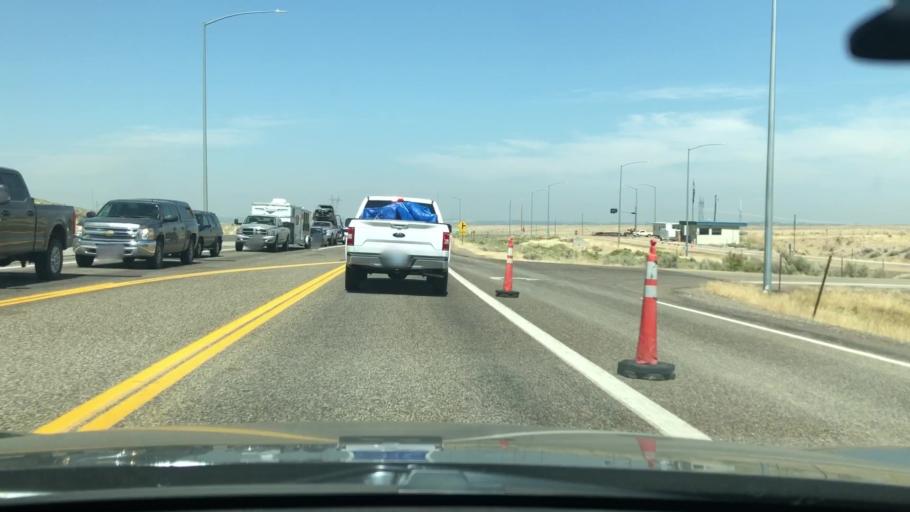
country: US
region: Idaho
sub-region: Owyhee County
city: Marsing
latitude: 43.4629
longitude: -116.8665
